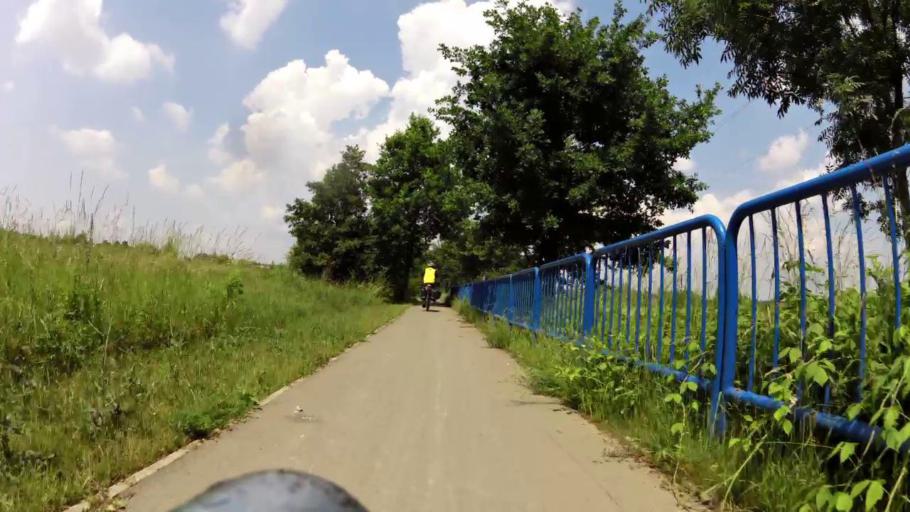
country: PL
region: Kujawsko-Pomorskie
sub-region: Powiat bydgoski
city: Koronowo
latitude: 53.2877
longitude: 17.9470
